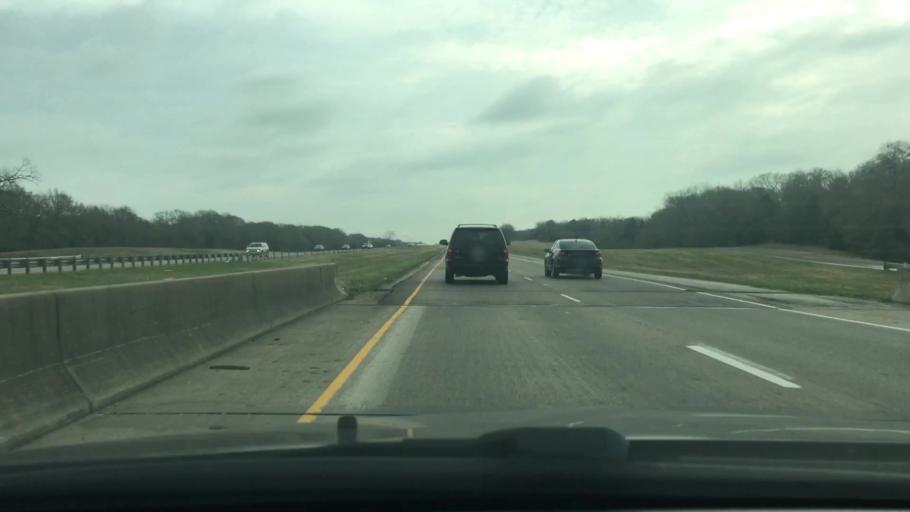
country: US
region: Texas
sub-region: Freestone County
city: Fairfield
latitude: 31.6268
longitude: -96.1577
